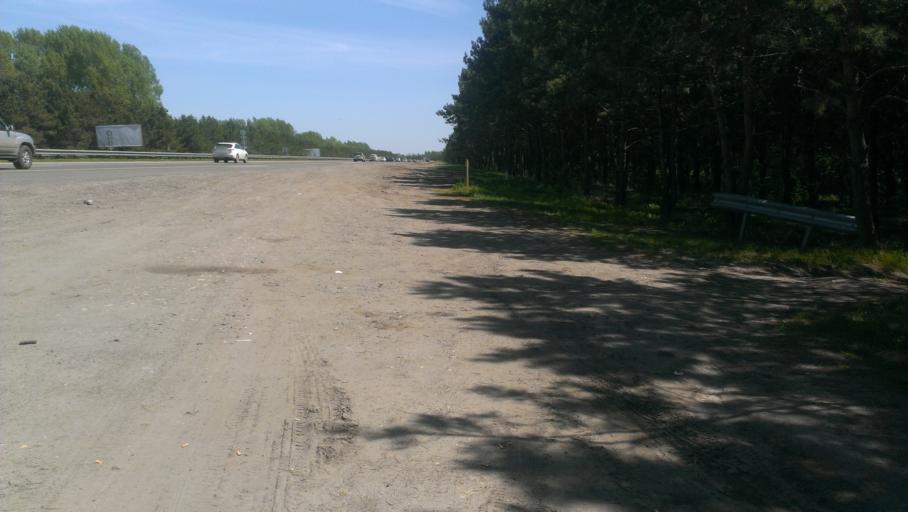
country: RU
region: Altai Krai
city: Zaton
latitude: 53.3150
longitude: 83.8418
